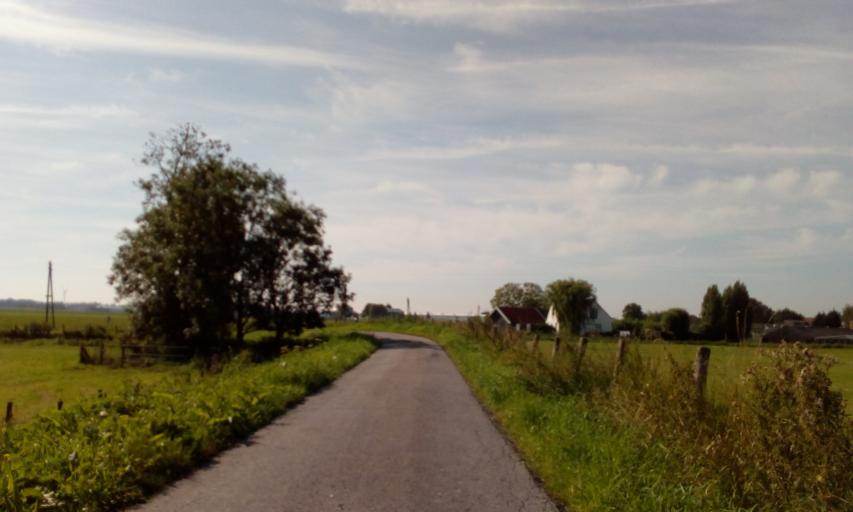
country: NL
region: South Holland
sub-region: Gemeente Waddinxveen
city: Groenswaard
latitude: 52.0472
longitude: 4.6098
